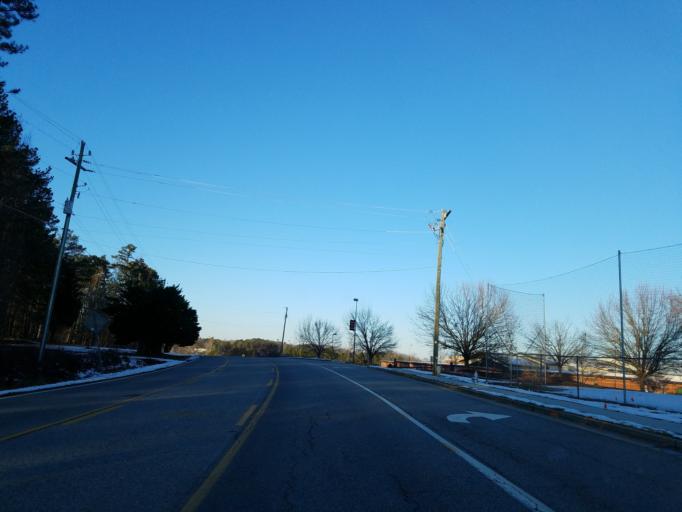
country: US
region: Georgia
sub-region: Dawson County
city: Dawsonville
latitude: 34.4124
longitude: -84.1055
